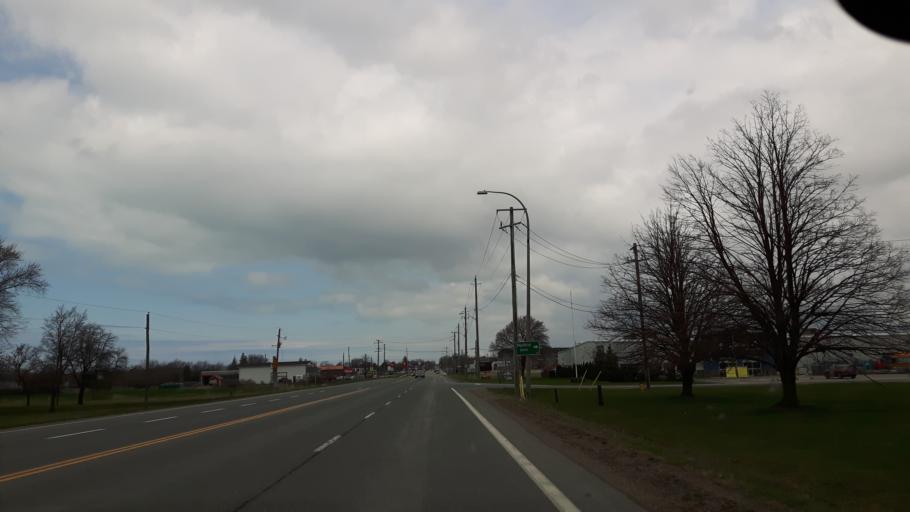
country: CA
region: Ontario
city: Goderich
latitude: 43.7259
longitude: -81.7058
